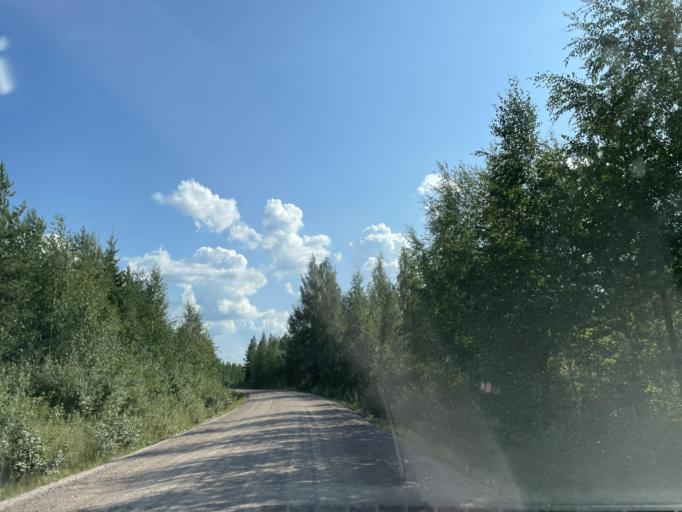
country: FI
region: Central Finland
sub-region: Saarijaervi-Viitasaari
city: Pihtipudas
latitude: 63.3482
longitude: 25.7898
